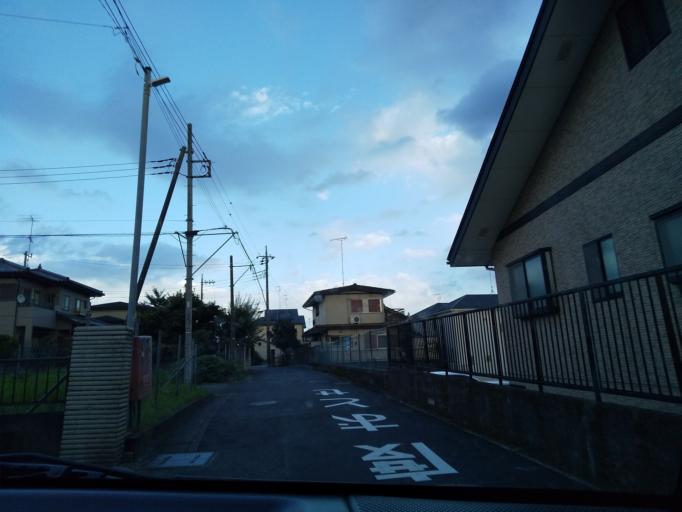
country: JP
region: Tokyo
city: Hachioji
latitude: 35.5942
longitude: 139.3049
